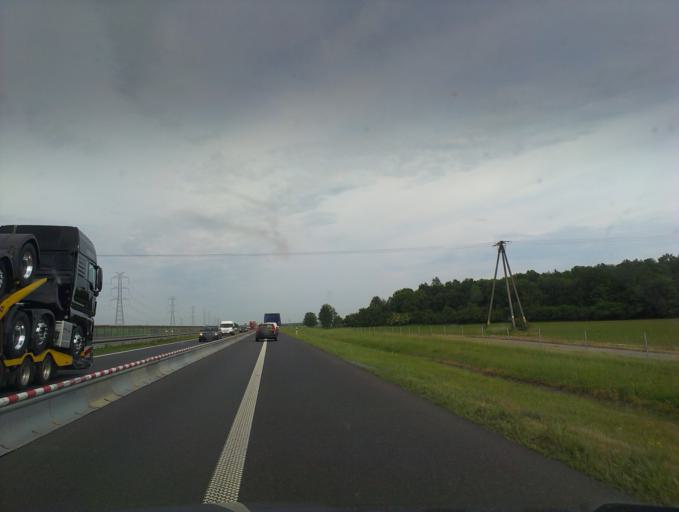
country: PL
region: Opole Voivodeship
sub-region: Powiat brzeski
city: Losiow
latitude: 50.7194
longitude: 17.5440
